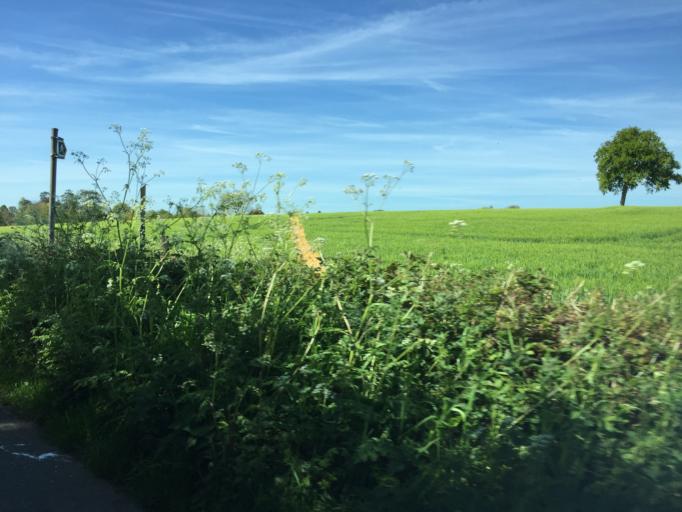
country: GB
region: England
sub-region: Wiltshire
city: Luckington
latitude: 51.5902
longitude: -2.2549
